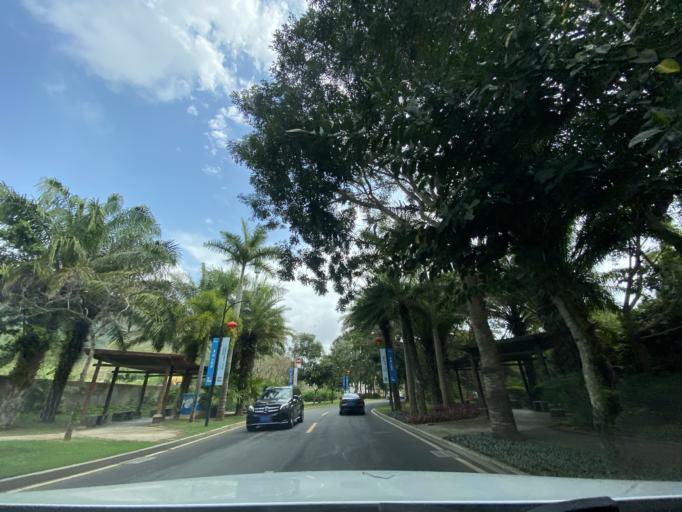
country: CN
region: Hainan
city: Liji
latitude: 18.6697
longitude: 110.2647
